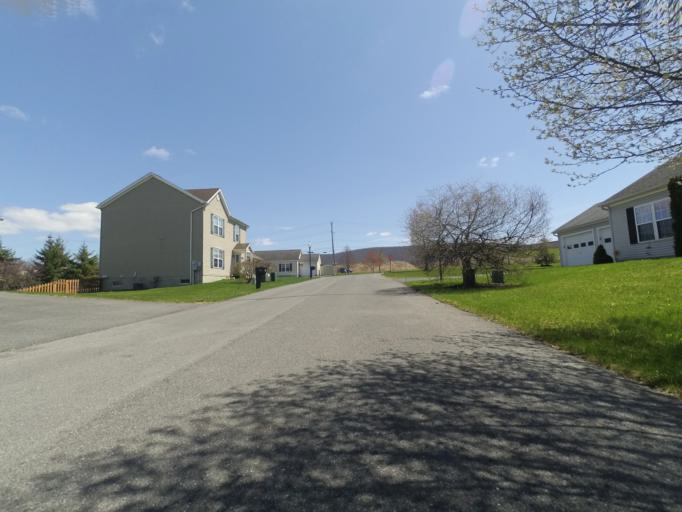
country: US
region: Pennsylvania
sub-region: Centre County
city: Houserville
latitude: 40.8365
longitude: -77.8075
